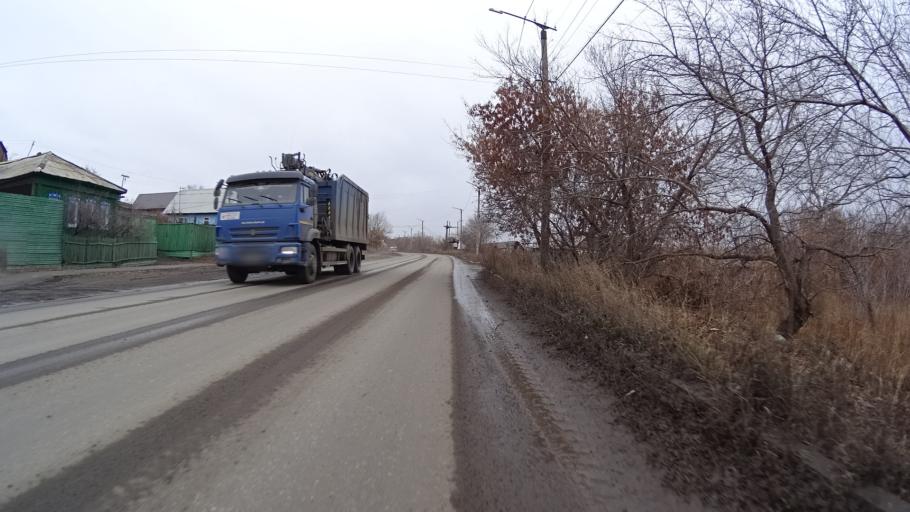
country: RU
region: Chelyabinsk
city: Troitsk
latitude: 54.0978
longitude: 61.5440
